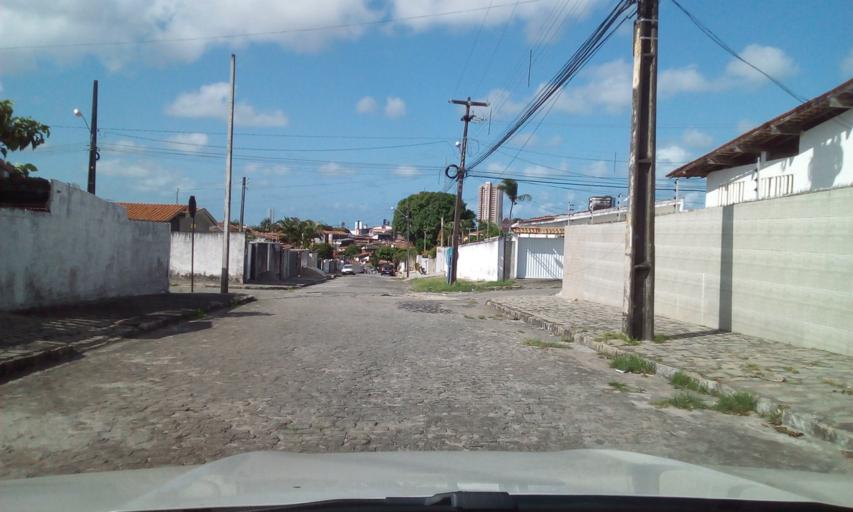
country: BR
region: Paraiba
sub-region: Joao Pessoa
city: Joao Pessoa
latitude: -7.1103
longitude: -34.8624
